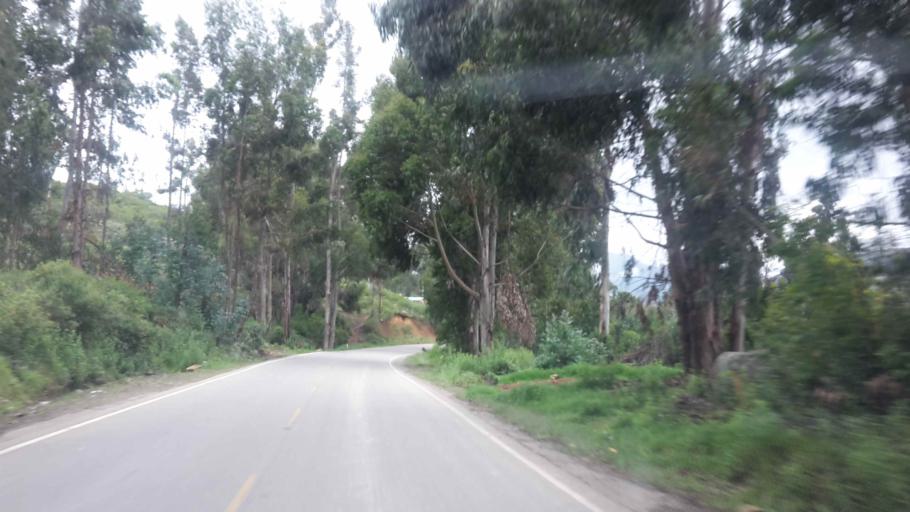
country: BO
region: Cochabamba
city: Totora
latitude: -17.5751
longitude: -65.3148
